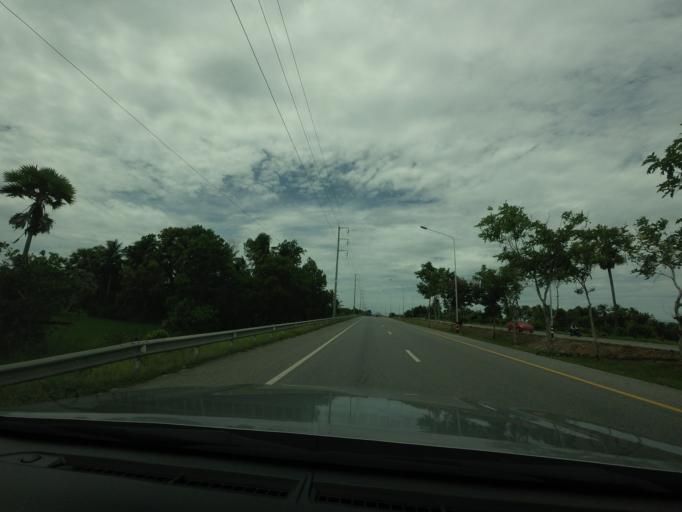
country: TH
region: Pattani
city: Pattani
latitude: 6.8472
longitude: 101.2245
